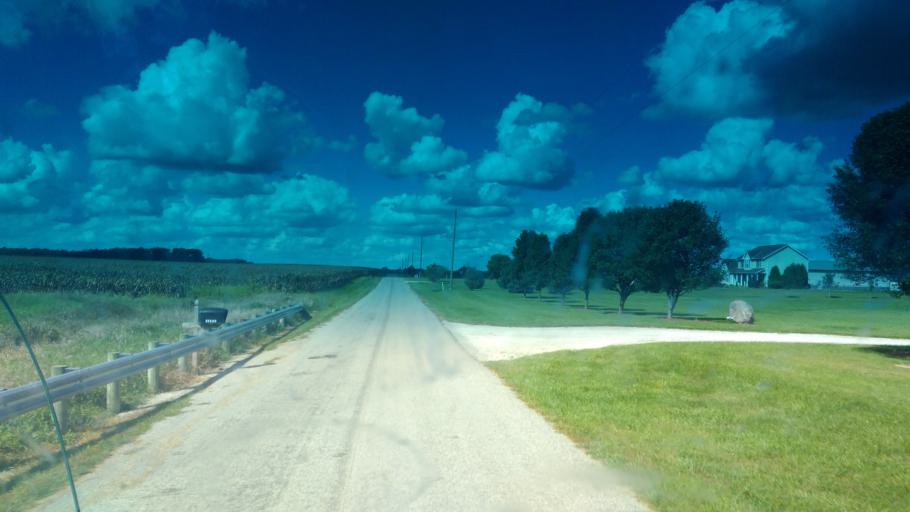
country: US
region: Ohio
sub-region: Union County
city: Richwood
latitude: 40.4671
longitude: -83.4962
